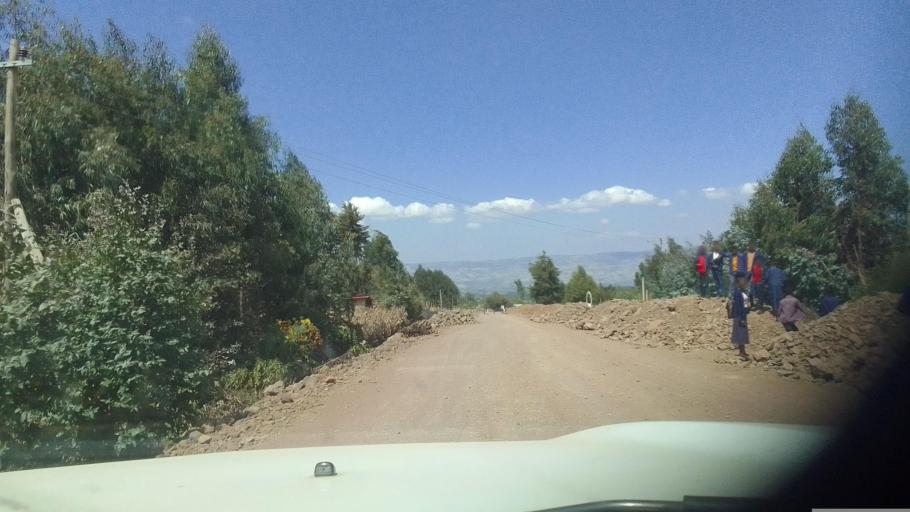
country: ET
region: Oromiya
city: Hagere Hiywet
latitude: 8.8595
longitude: 37.8910
